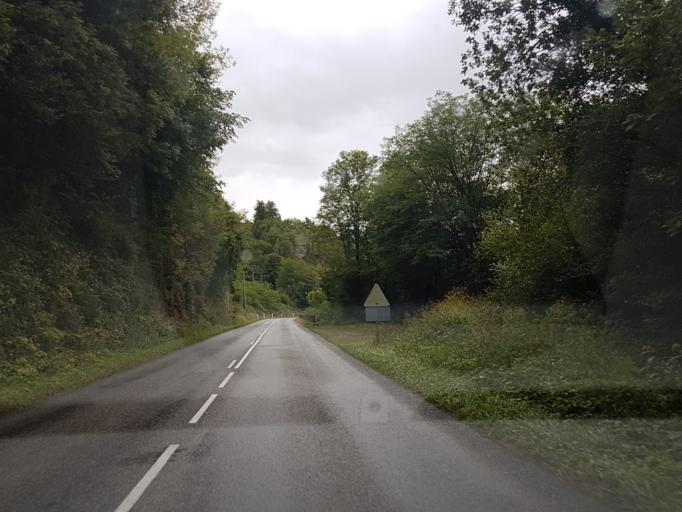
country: FR
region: Midi-Pyrenees
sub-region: Departement de l'Ariege
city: Saint-Girons
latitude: 42.8953
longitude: 1.2152
